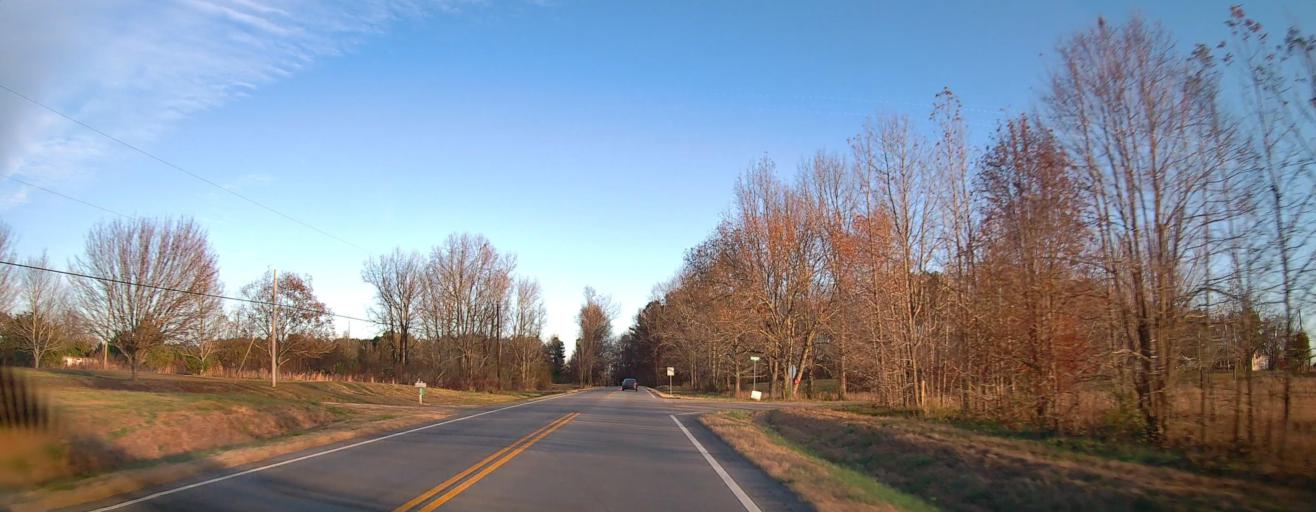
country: US
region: Alabama
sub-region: Saint Clair County
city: Steele
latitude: 34.0611
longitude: -86.2369
